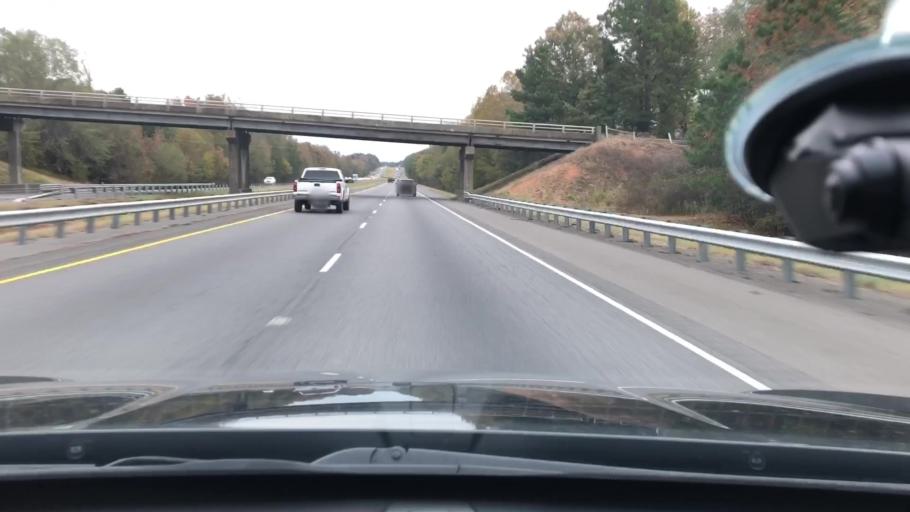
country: US
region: Arkansas
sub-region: Clark County
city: Gurdon
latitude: 34.0214
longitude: -93.1583
